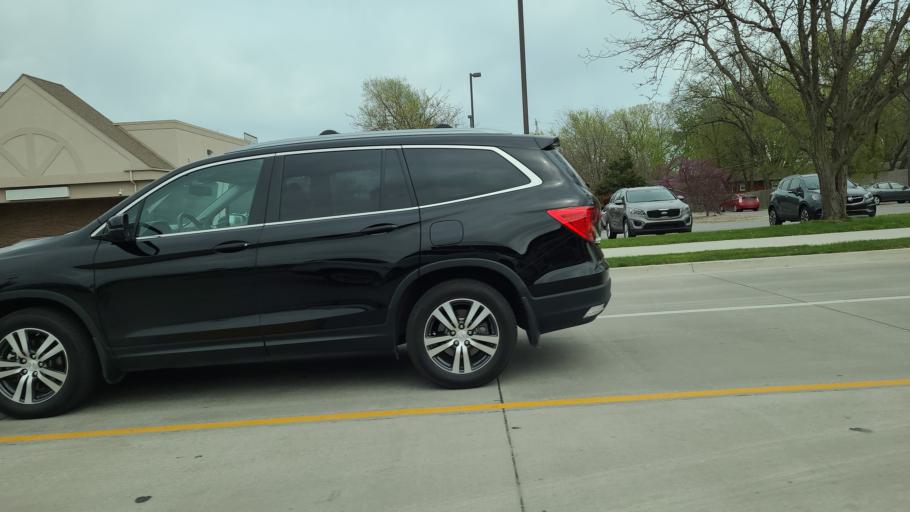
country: US
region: Kansas
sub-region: Douglas County
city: Lawrence
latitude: 38.9709
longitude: -95.2813
